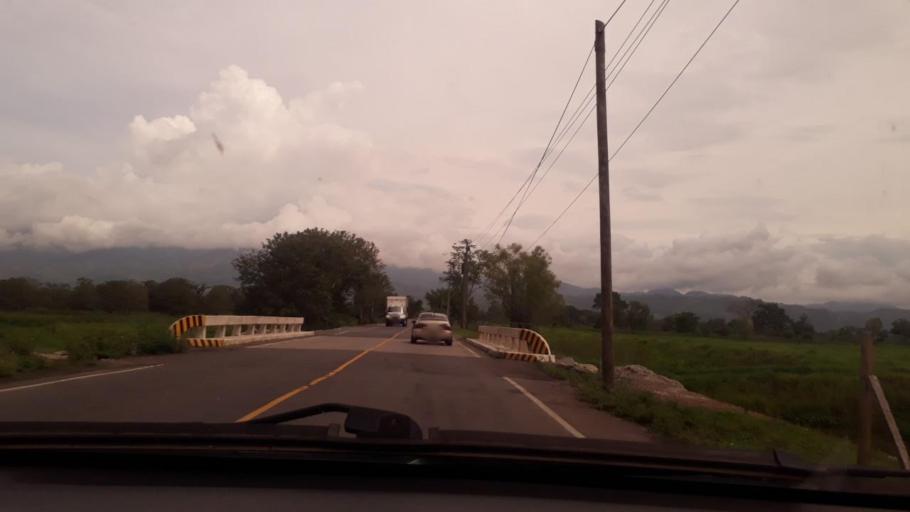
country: HN
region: Cortes
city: Potrerillos
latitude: 15.6245
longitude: -88.4010
